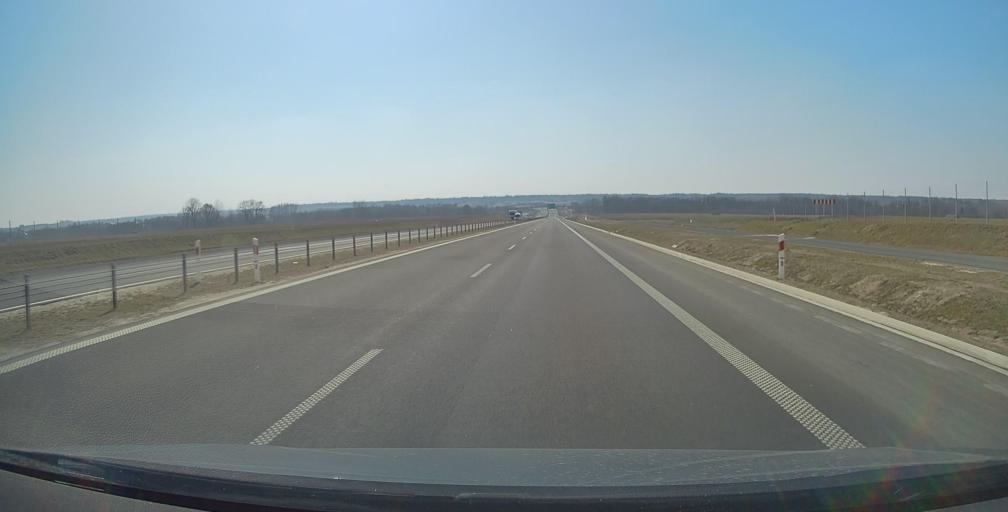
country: PL
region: Lublin Voivodeship
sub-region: Powiat janowski
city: Modliborzyce
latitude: 50.7657
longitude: 22.2914
